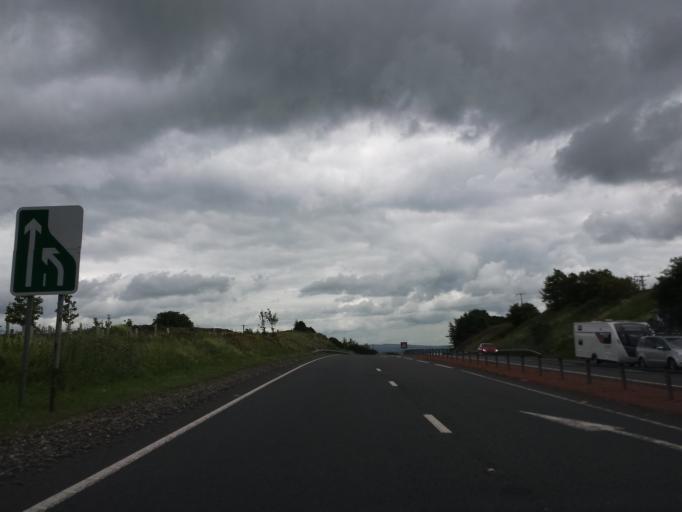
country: GB
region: Scotland
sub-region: Dumfries and Galloway
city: Dumfries
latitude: 55.0593
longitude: -3.6894
